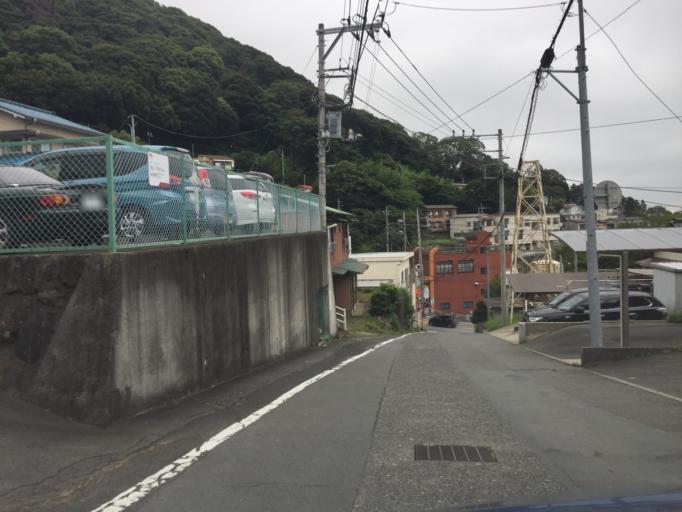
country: JP
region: Shizuoka
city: Atami
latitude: 35.1140
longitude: 139.0794
